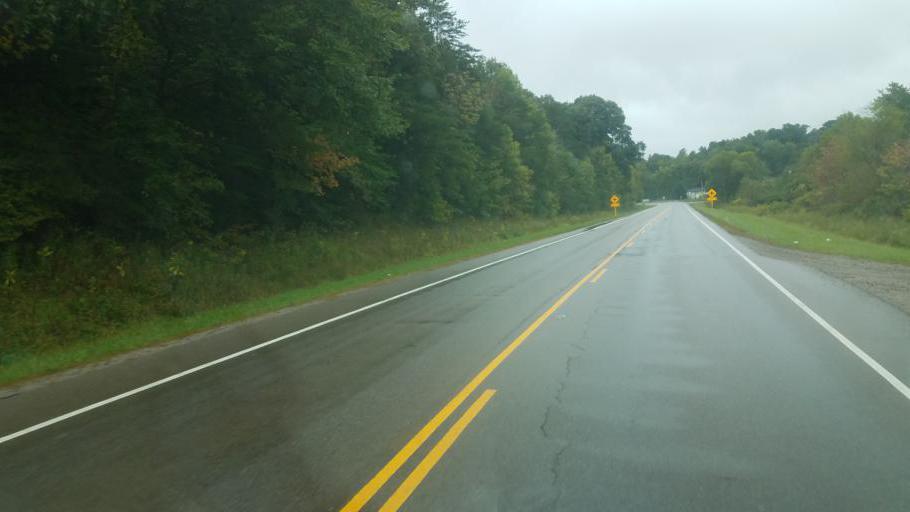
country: US
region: Ohio
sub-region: Jackson County
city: Oak Hill
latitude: 38.8627
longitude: -82.5987
